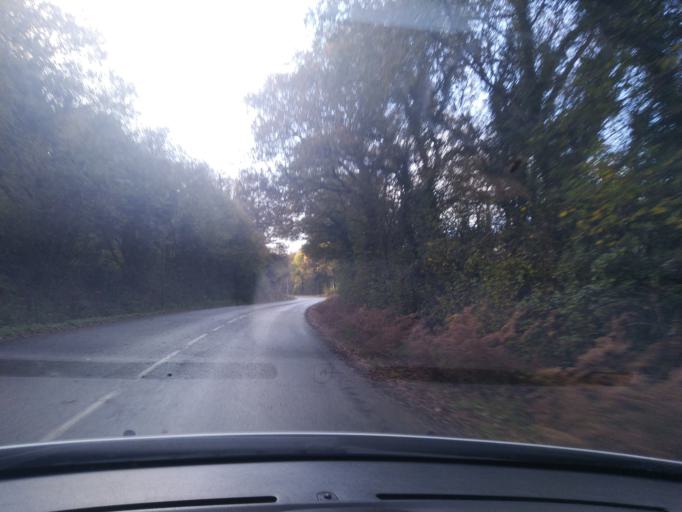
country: FR
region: Brittany
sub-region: Departement du Finistere
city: Plouigneau
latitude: 48.5715
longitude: -3.6621
